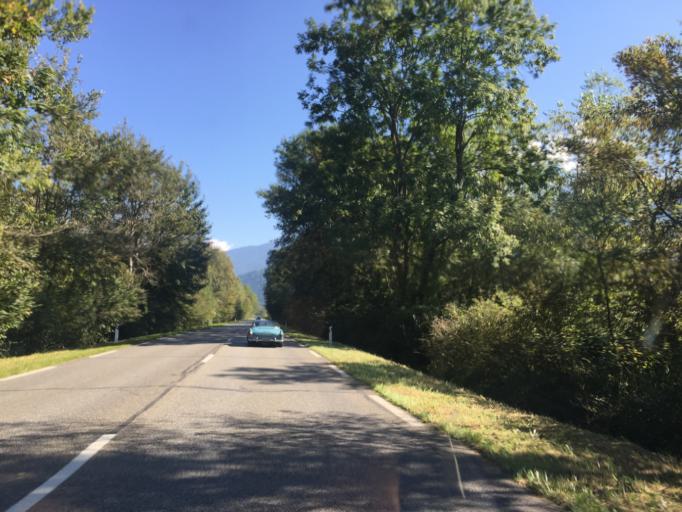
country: FR
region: Rhone-Alpes
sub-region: Departement de la Savoie
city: Aiton
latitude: 45.5782
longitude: 6.2528
